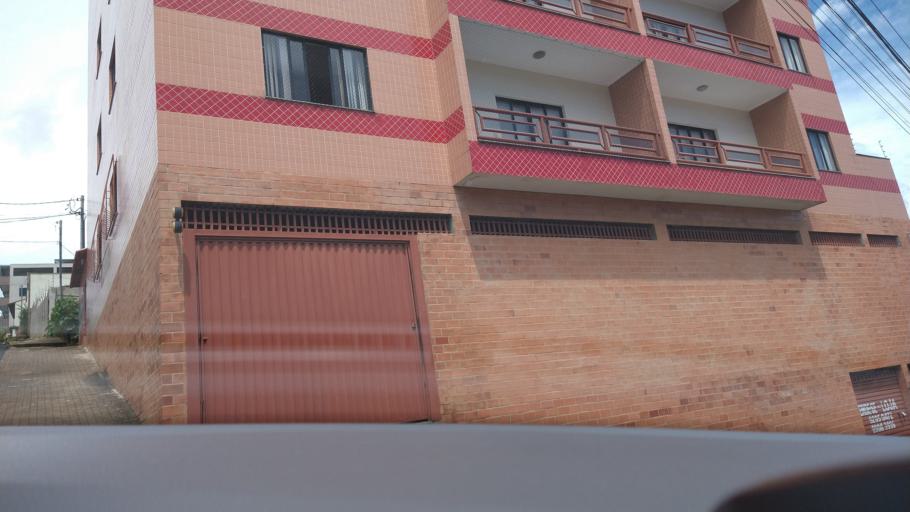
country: BR
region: Minas Gerais
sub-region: Vicosa
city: Vicosa
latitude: -20.7625
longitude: -42.8863
